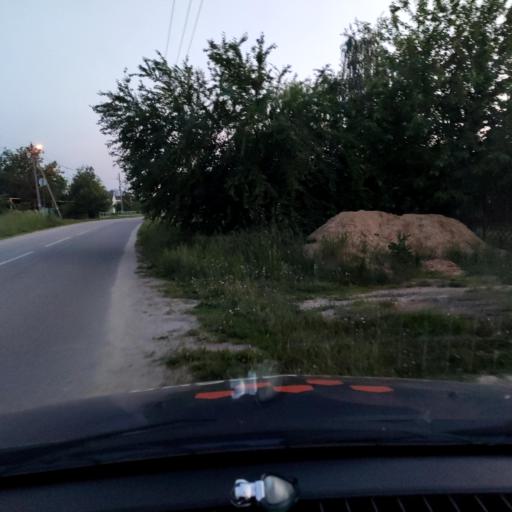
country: RU
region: Voronezj
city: Ramon'
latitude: 51.8128
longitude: 39.2615
